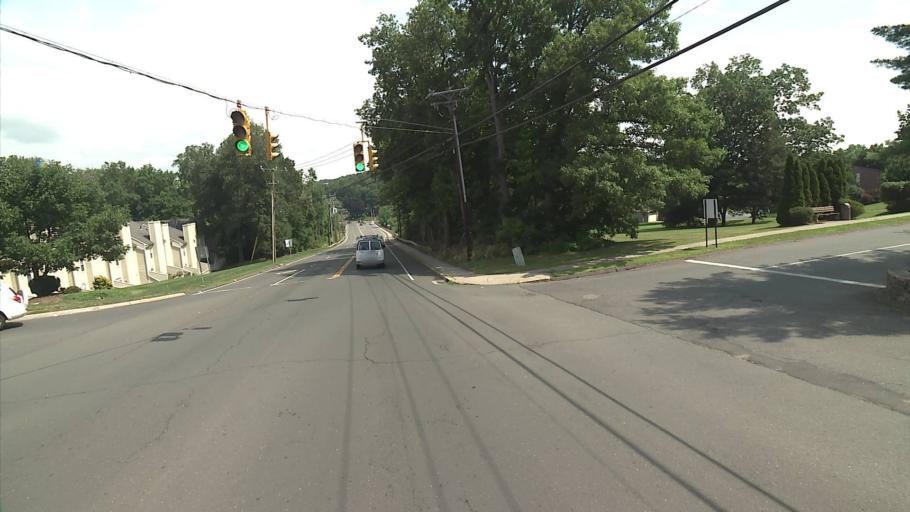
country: US
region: Connecticut
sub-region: Middlesex County
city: Cromwell
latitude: 41.5988
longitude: -72.6951
